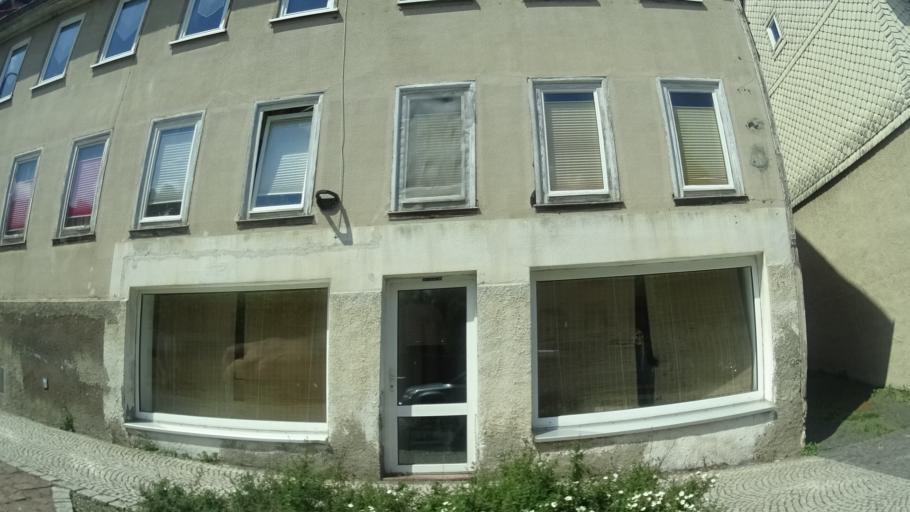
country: DE
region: Thuringia
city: Tambach-Dietharz
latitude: 50.7932
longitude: 10.6123
